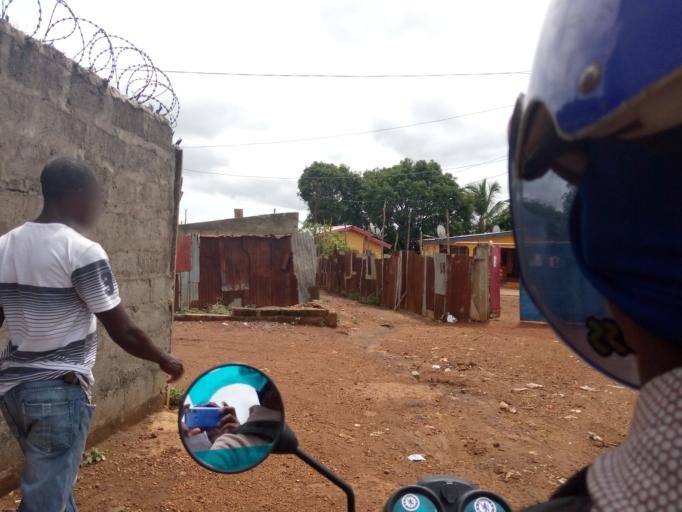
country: SL
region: Western Area
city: Hastings
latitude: 8.4141
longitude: -13.1412
